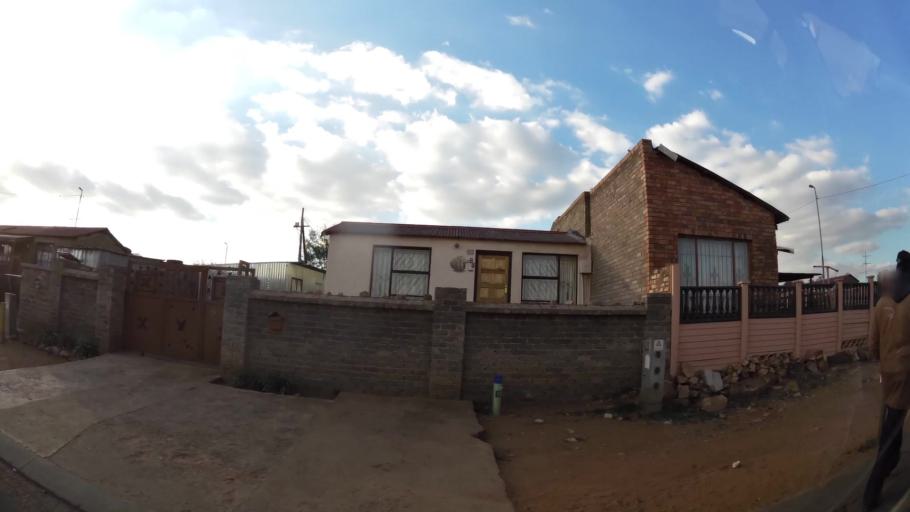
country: ZA
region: Gauteng
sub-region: West Rand District Municipality
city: Krugersdorp
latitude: -26.0740
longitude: 27.7576
